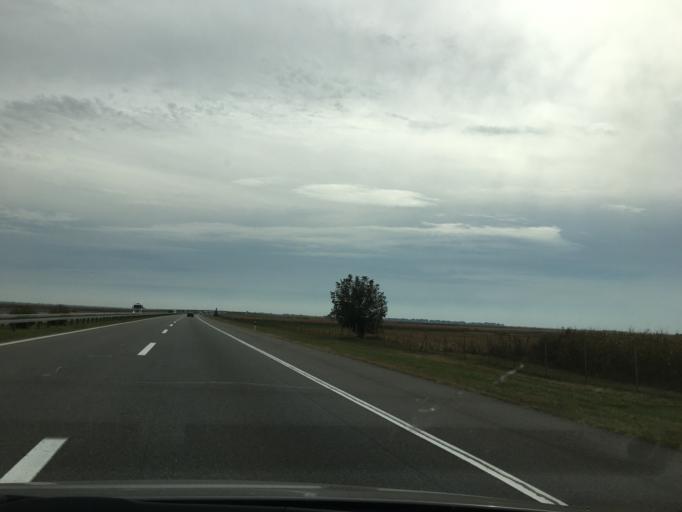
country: RS
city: Novi Karlovci
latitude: 45.0575
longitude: 20.1666
